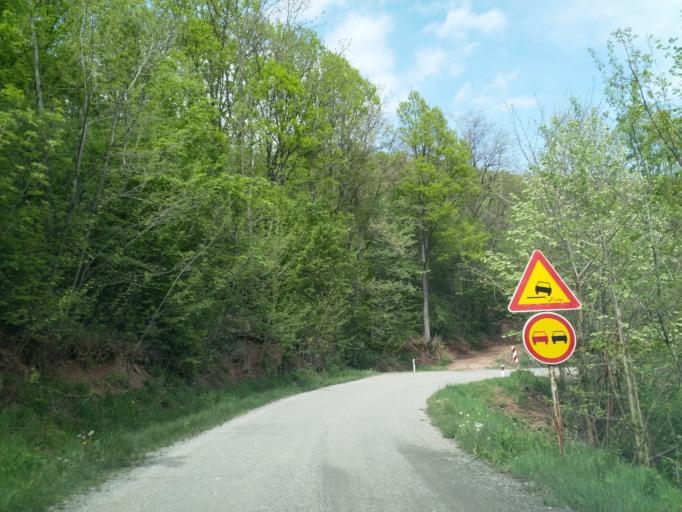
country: RS
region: Central Serbia
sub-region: Pomoravski Okrug
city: Despotovac
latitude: 43.9622
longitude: 21.5607
